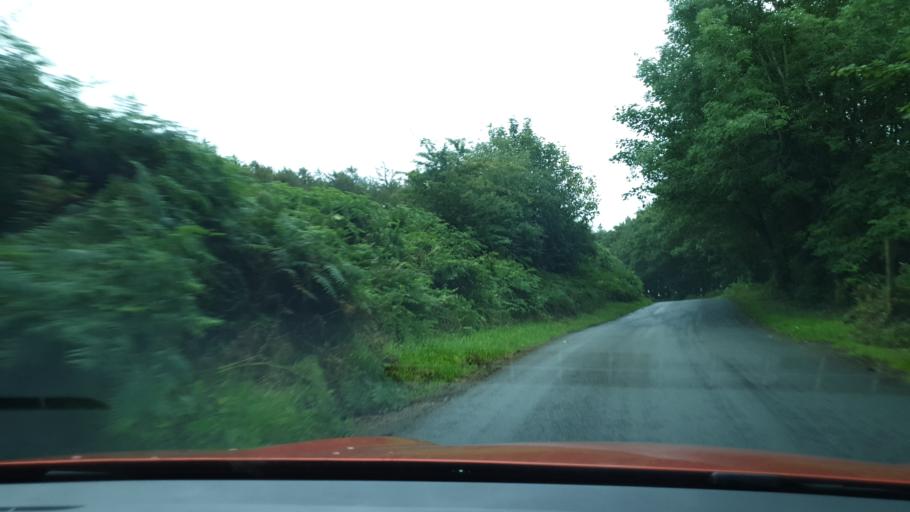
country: GB
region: England
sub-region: Cumbria
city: Seascale
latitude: 54.4005
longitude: -3.3646
